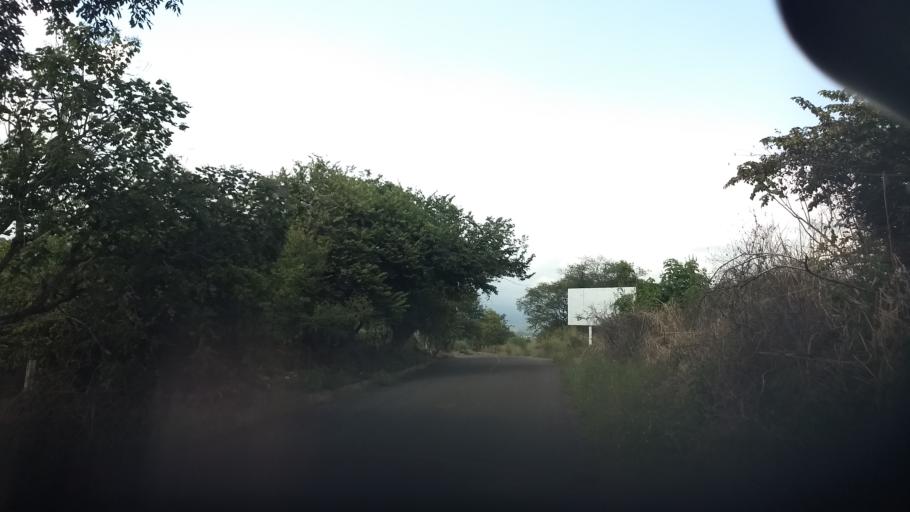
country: MX
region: Jalisco
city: Tonila
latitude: 19.4125
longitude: -103.4872
